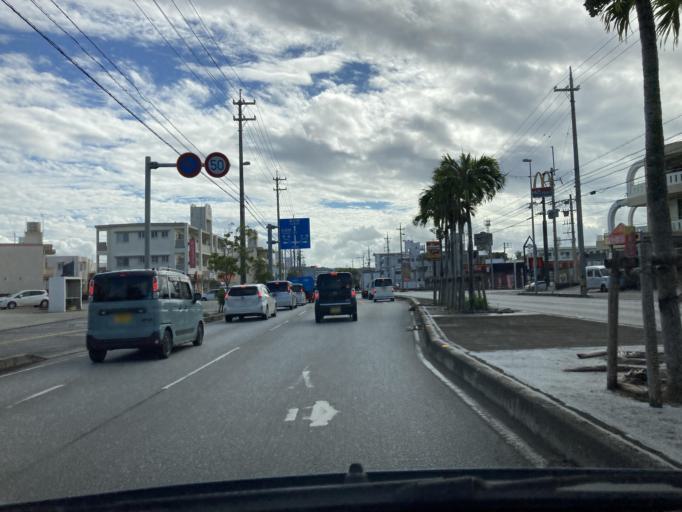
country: JP
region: Okinawa
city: Tomigusuku
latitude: 26.1582
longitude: 127.7218
